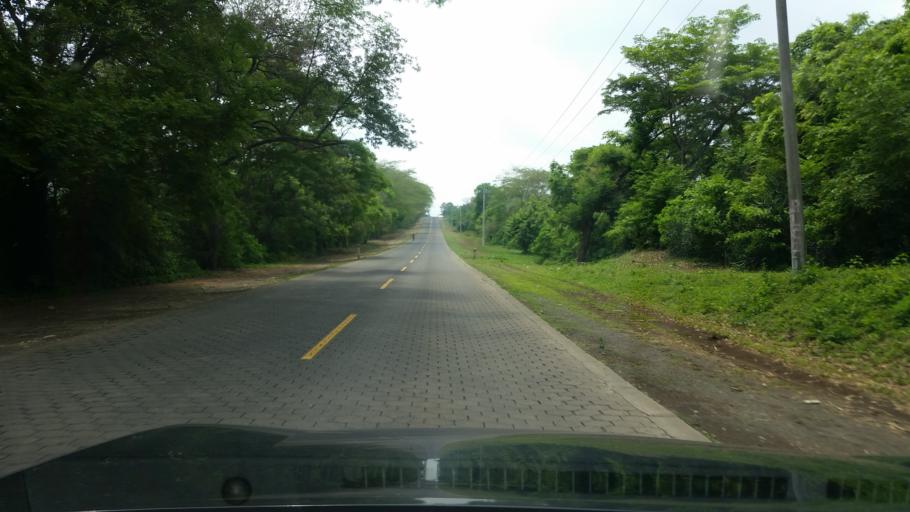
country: NI
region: Managua
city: San Rafael del Sur
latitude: 11.8883
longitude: -86.5142
